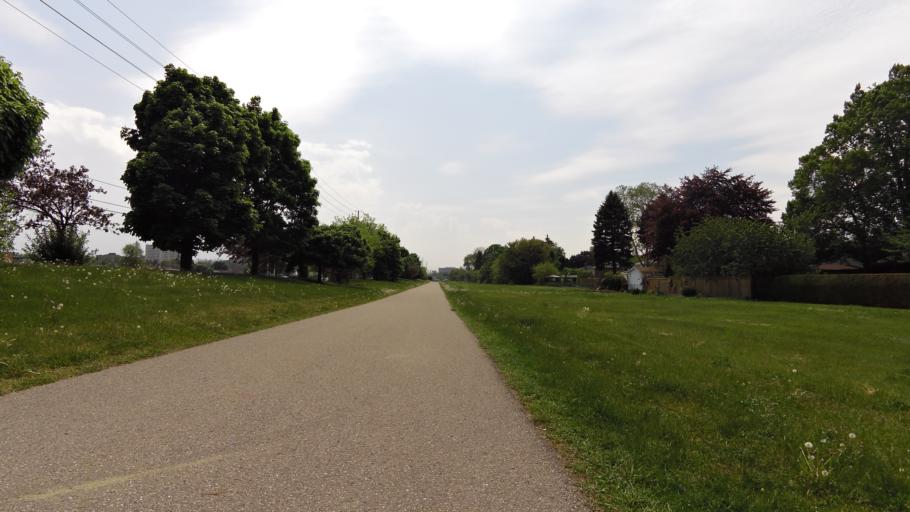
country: CA
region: Ontario
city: Mississauga
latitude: 43.5806
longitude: -79.6007
